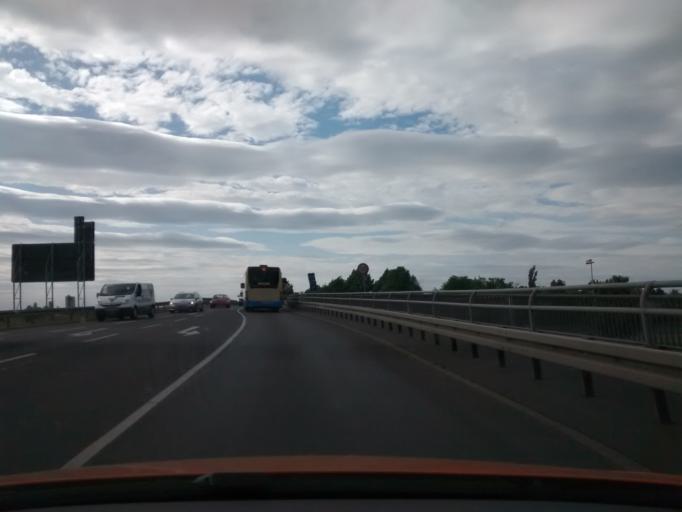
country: DE
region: Brandenburg
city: Schulzendorf
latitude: 52.3660
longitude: 13.5545
